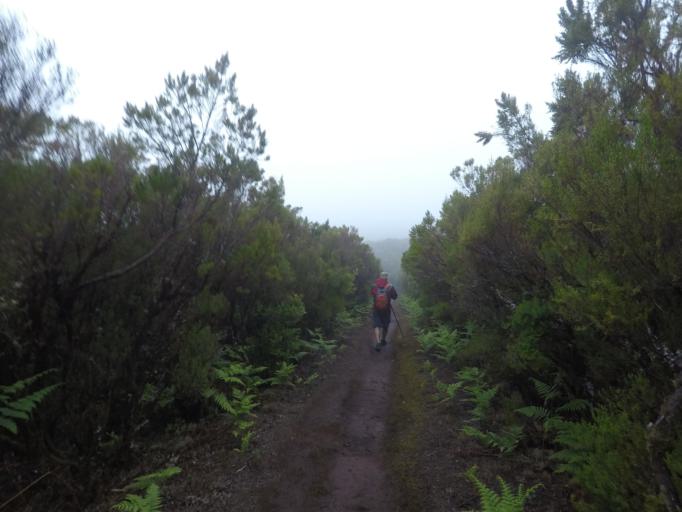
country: PT
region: Madeira
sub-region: Calheta
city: Arco da Calheta
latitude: 32.7722
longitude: -17.1242
